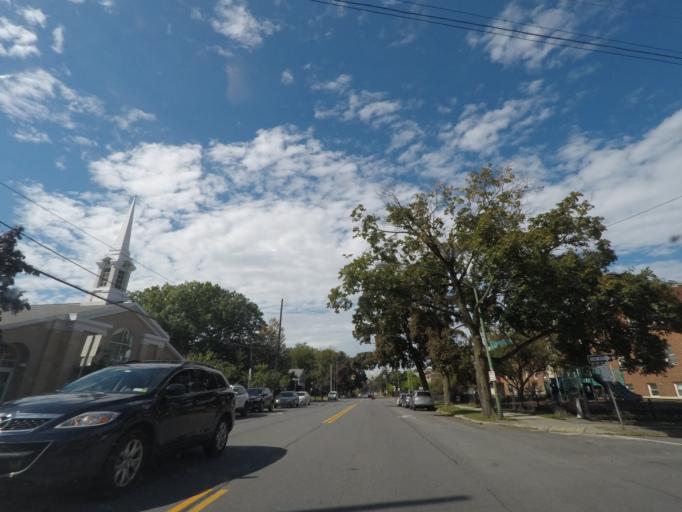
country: US
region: New York
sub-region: Albany County
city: West Albany
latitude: 42.6539
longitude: -73.7934
